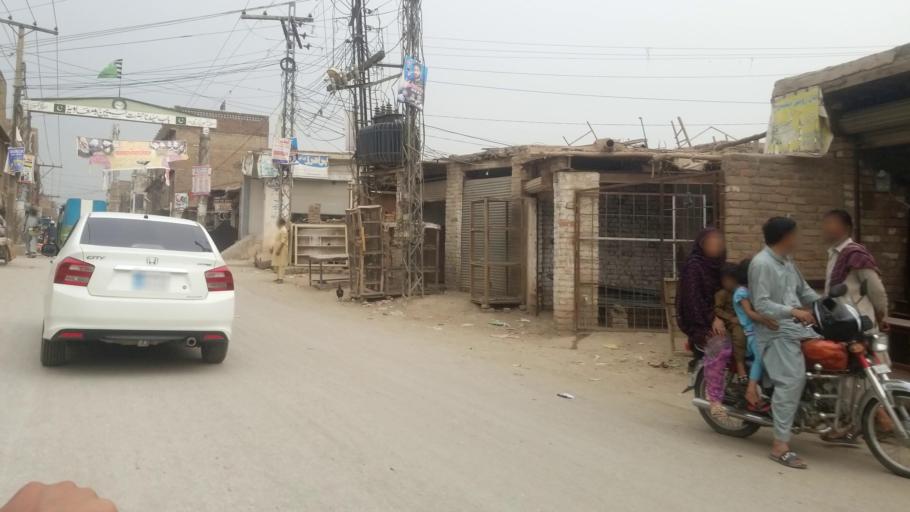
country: PK
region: Khyber Pakhtunkhwa
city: Peshawar
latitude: 33.9902
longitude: 71.5482
